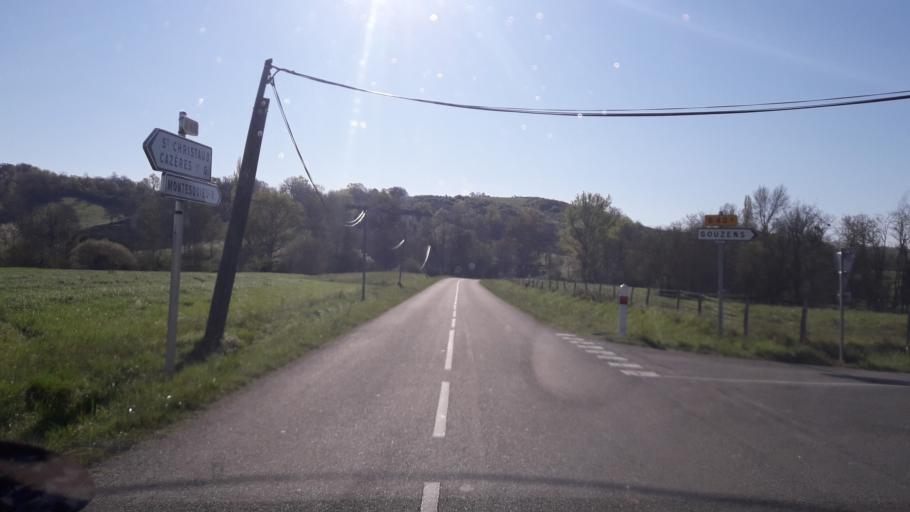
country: FR
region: Midi-Pyrenees
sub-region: Departement de la Haute-Garonne
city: Rieux-Volvestre
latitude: 43.2018
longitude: 1.1735
